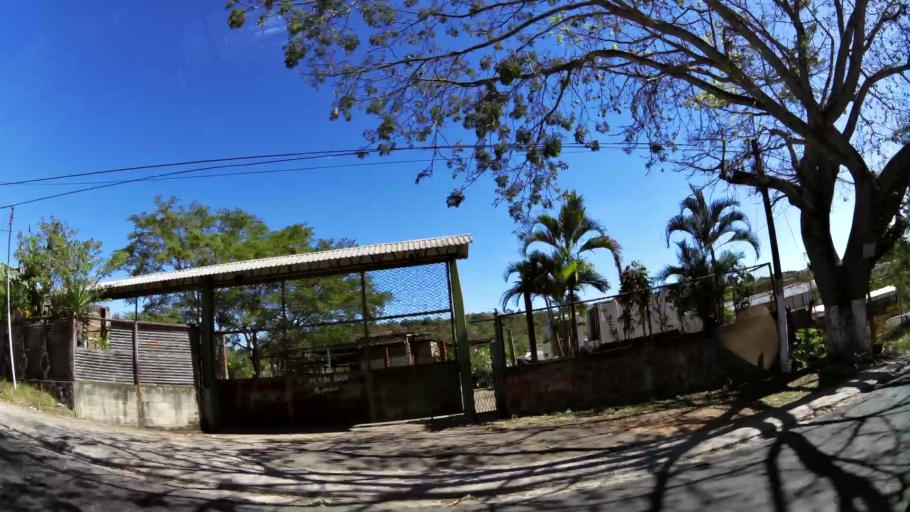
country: SV
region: La Libertad
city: San Juan Opico
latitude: 13.8675
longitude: -89.3604
